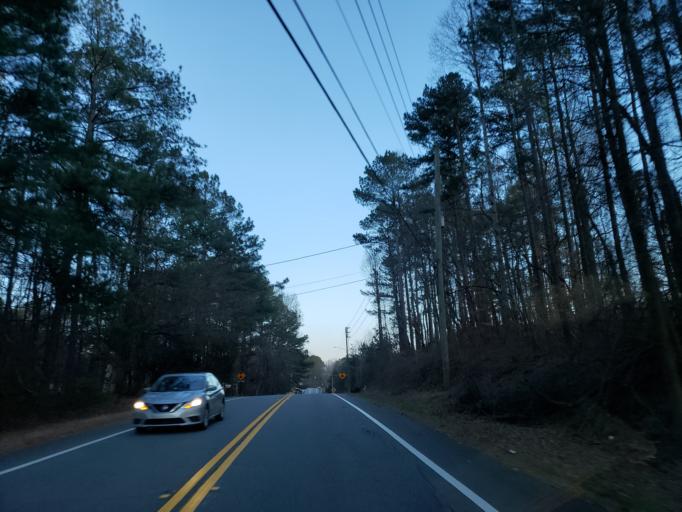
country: US
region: Georgia
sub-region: Cobb County
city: Acworth
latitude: 33.9873
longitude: -84.6962
